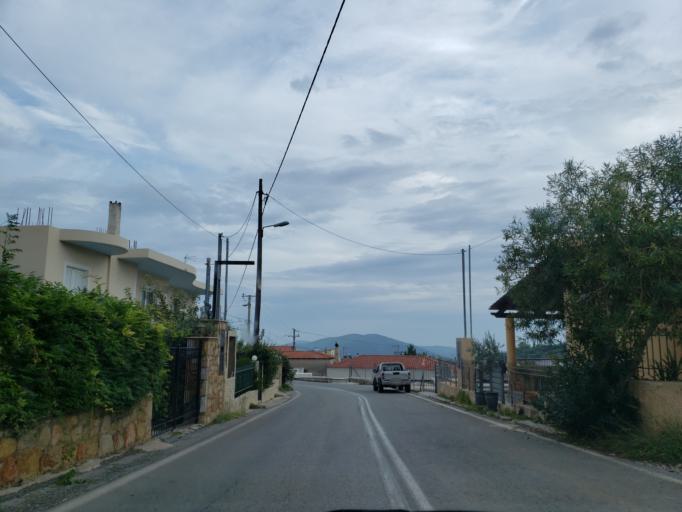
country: GR
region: Attica
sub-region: Nomarchia Anatolikis Attikis
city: Grammatiko
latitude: 38.2036
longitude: 23.9626
